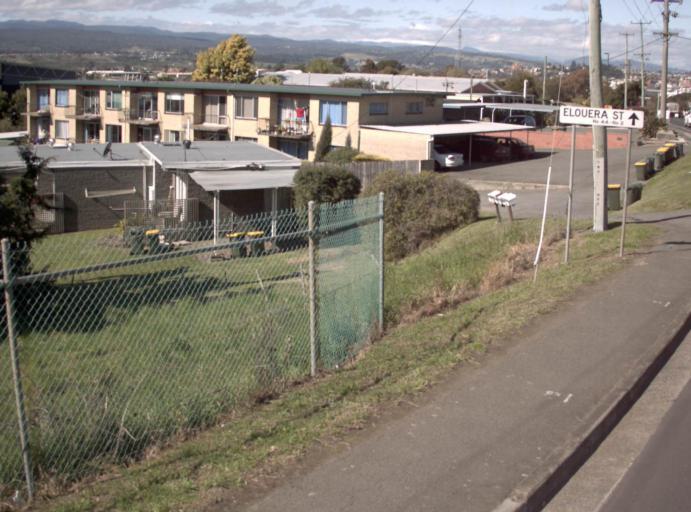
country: AU
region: Tasmania
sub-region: Launceston
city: Launceston
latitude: -41.4207
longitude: 147.1095
